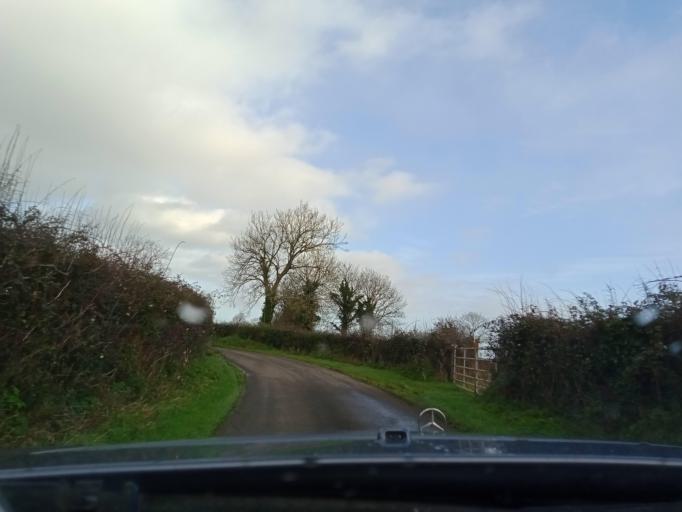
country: IE
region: Leinster
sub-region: Kilkenny
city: Callan
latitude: 52.4871
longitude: -7.3633
